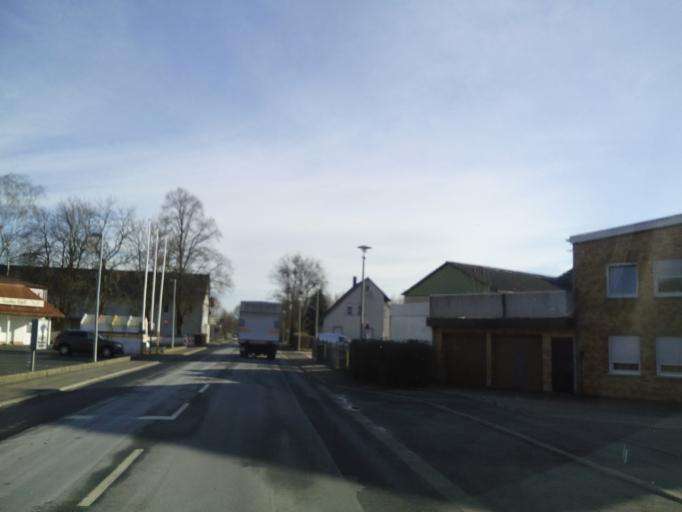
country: DE
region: Bavaria
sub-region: Upper Franconia
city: Marktzeuln
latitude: 50.1654
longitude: 11.1720
